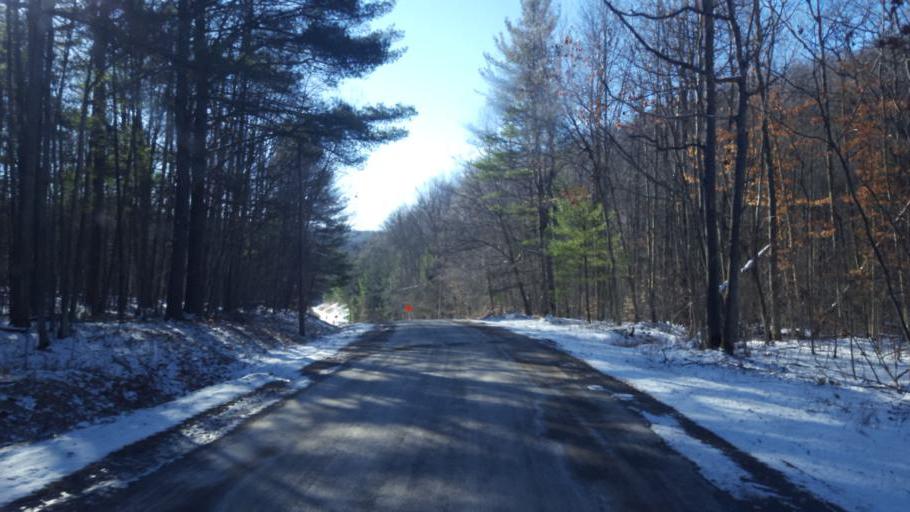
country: US
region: New York
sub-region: Allegany County
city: Wellsville
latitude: 42.1503
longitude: -77.9098
